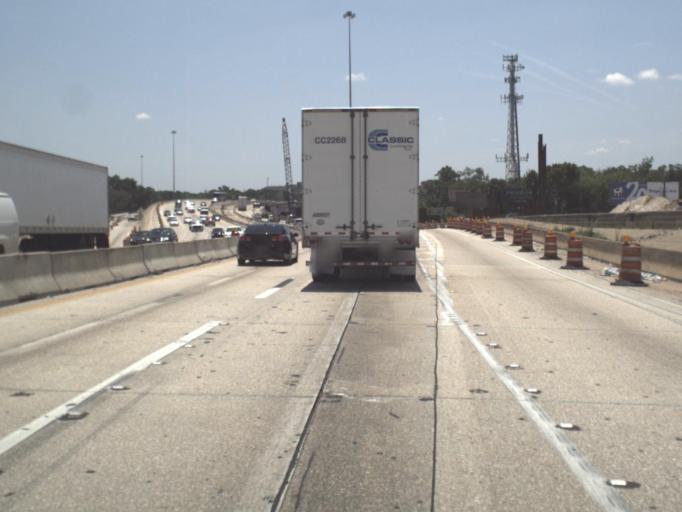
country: US
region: Florida
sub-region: Duval County
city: Jacksonville
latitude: 30.3122
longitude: -81.6506
